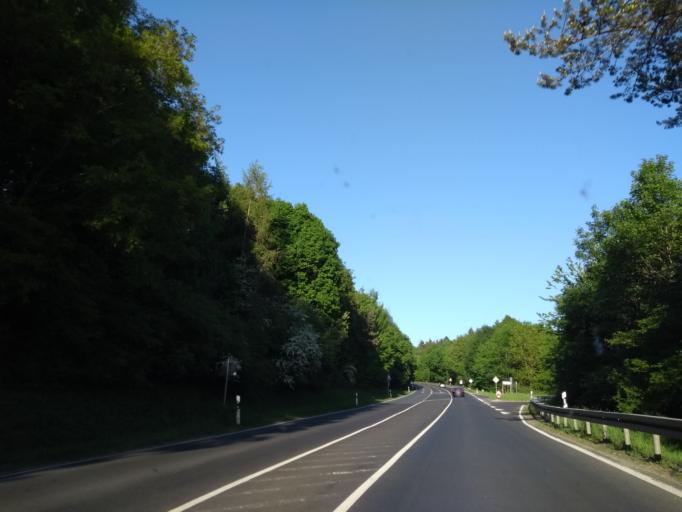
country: DE
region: Hesse
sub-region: Regierungsbezirk Darmstadt
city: Friedrichsdorf
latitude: 50.2812
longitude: 8.6295
